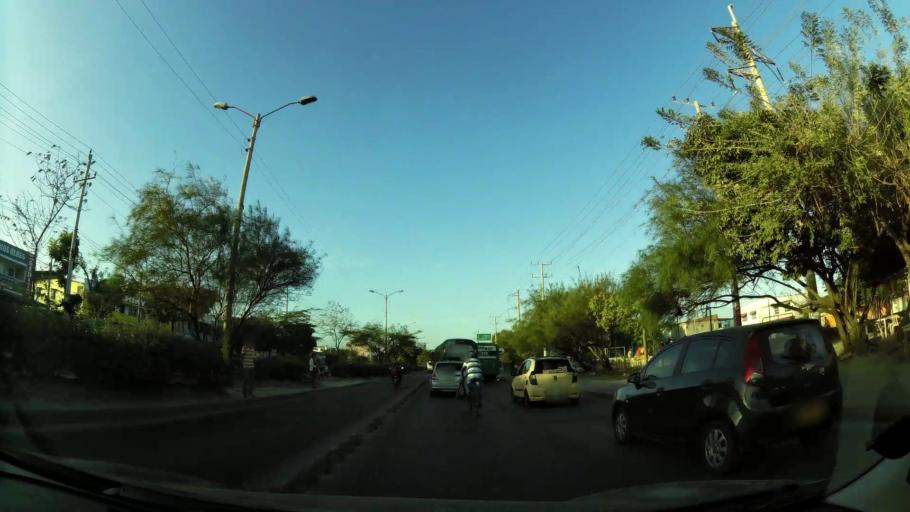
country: CO
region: Atlantico
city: Soledad
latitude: 10.9184
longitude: -74.7991
